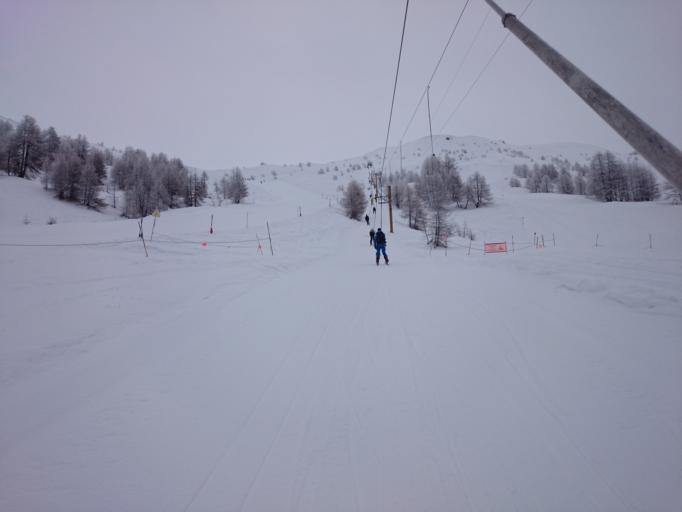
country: IT
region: Piedmont
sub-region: Provincia di Torino
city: Prali
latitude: 44.7942
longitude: 6.9539
